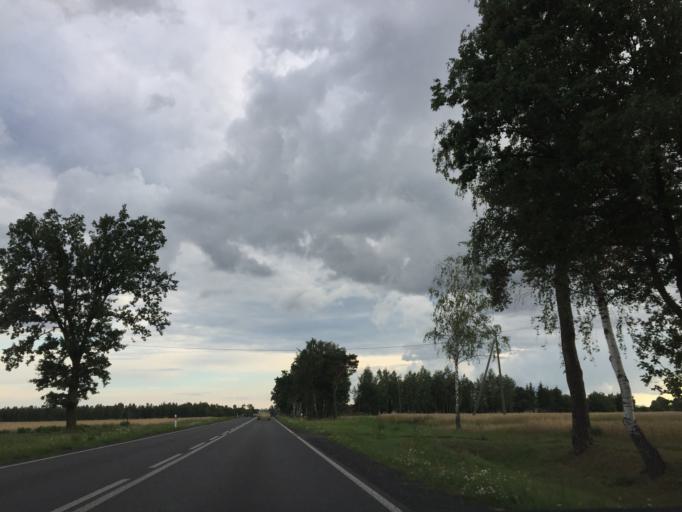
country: PL
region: Lublin Voivodeship
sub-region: Powiat radzynski
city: Borki
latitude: 51.6802
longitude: 22.4889
